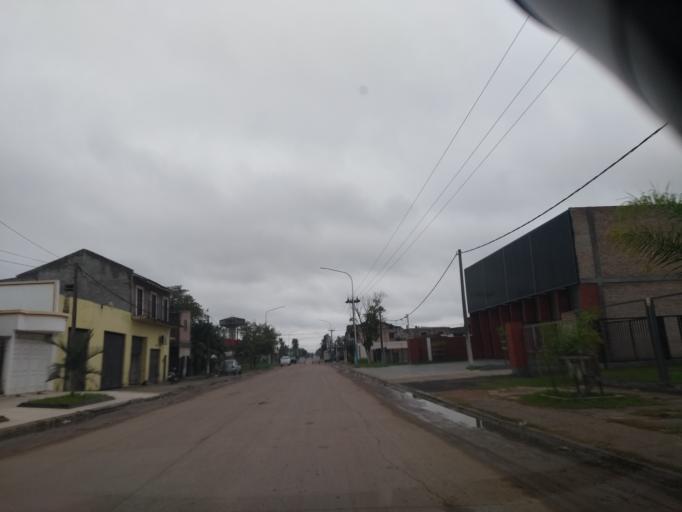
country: AR
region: Chaco
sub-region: Departamento de Quitilipi
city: Quitilipi
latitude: -26.8769
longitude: -60.2198
